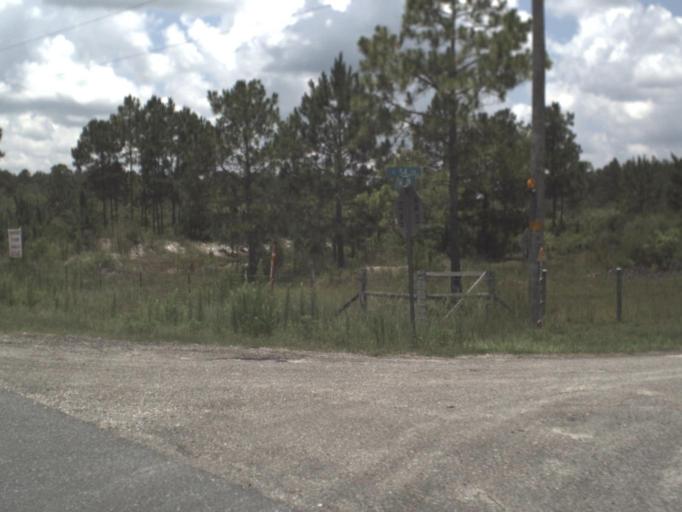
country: US
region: Florida
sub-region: Gilchrist County
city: Trenton
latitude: 29.6293
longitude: -82.7156
